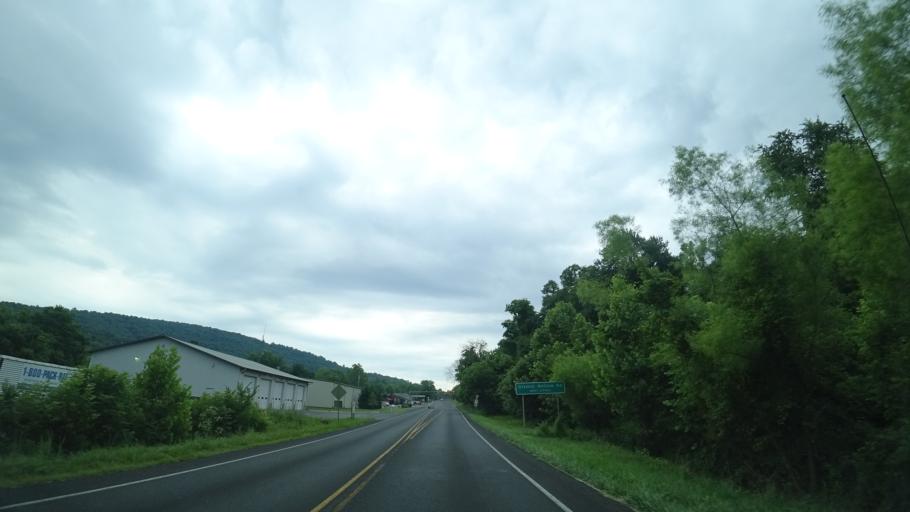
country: US
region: Virginia
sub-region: Warren County
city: Apple Mountain Lake
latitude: 38.9138
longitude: -78.1045
